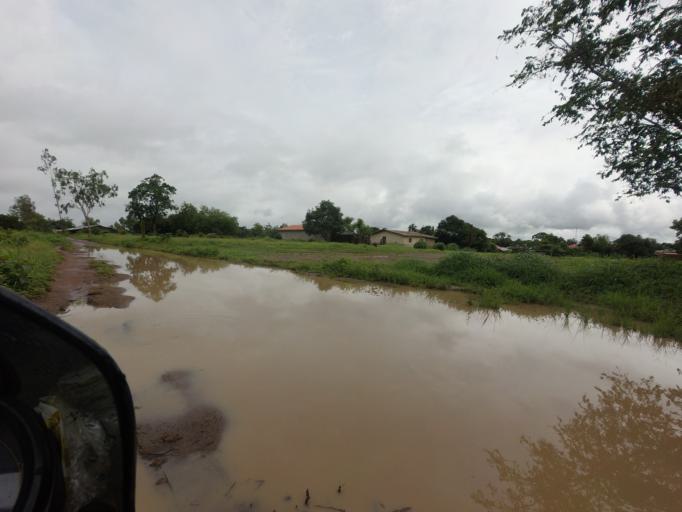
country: SL
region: Northern Province
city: Kambia
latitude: 9.1040
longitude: -12.9288
